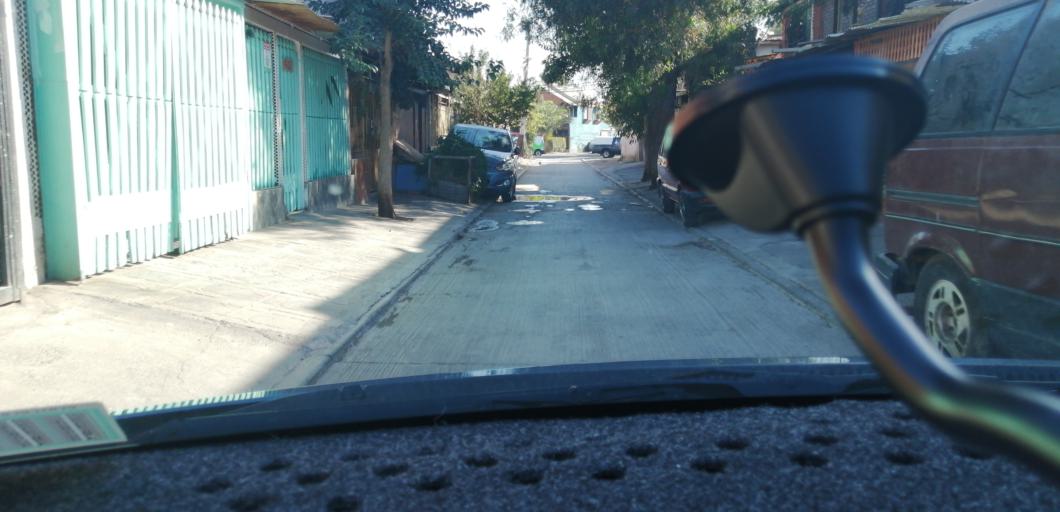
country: CL
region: Santiago Metropolitan
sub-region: Provincia de Santiago
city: Lo Prado
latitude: -33.4282
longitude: -70.7659
